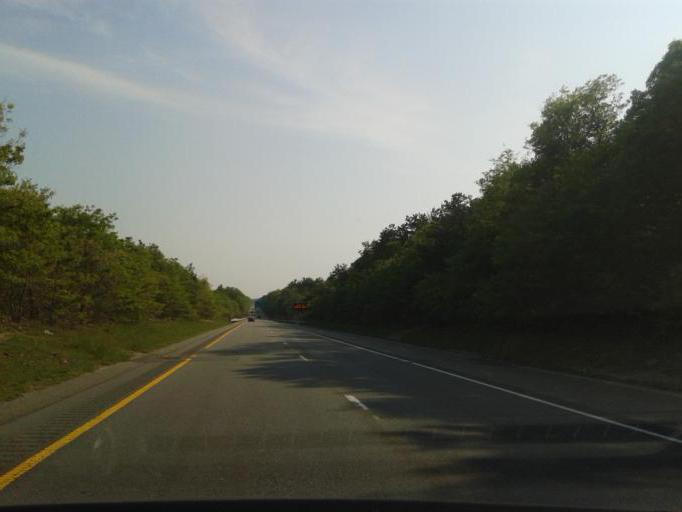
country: US
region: Massachusetts
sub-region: Barnstable County
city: North Falmouth
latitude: 41.6329
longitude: -70.6110
